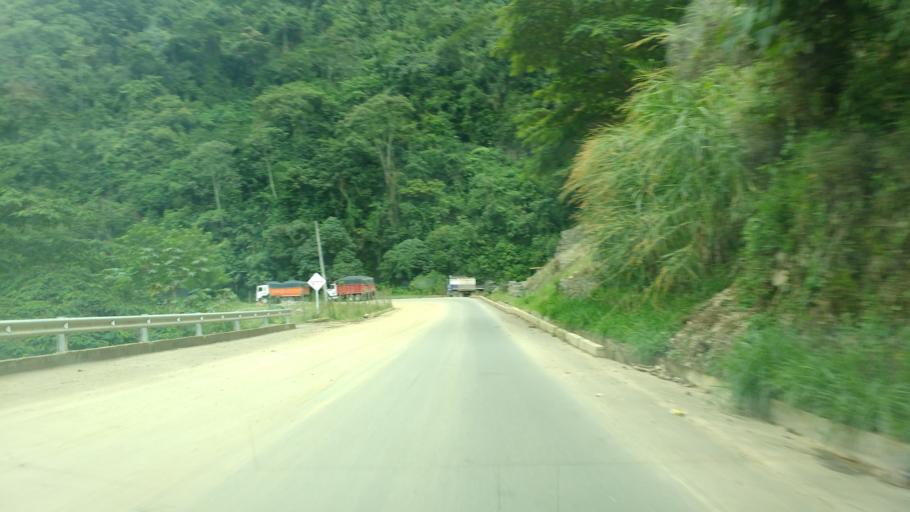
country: CO
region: Antioquia
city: Amaga
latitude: 6.0486
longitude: -75.7163
